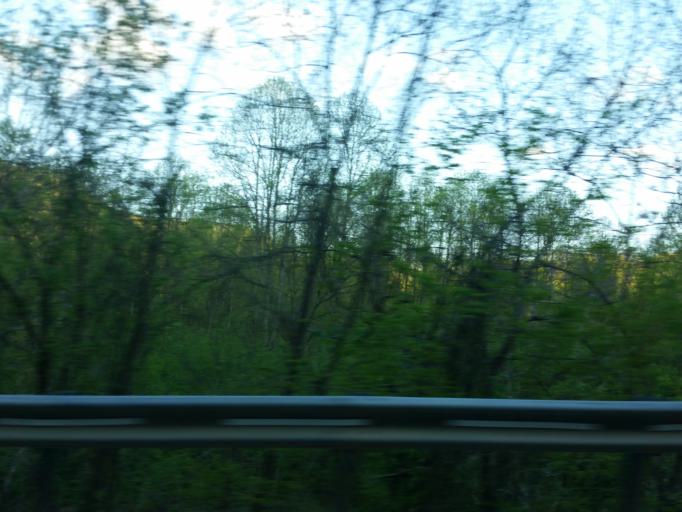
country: US
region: Tennessee
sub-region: Campbell County
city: Jellico
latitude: 36.5559
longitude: -83.9699
